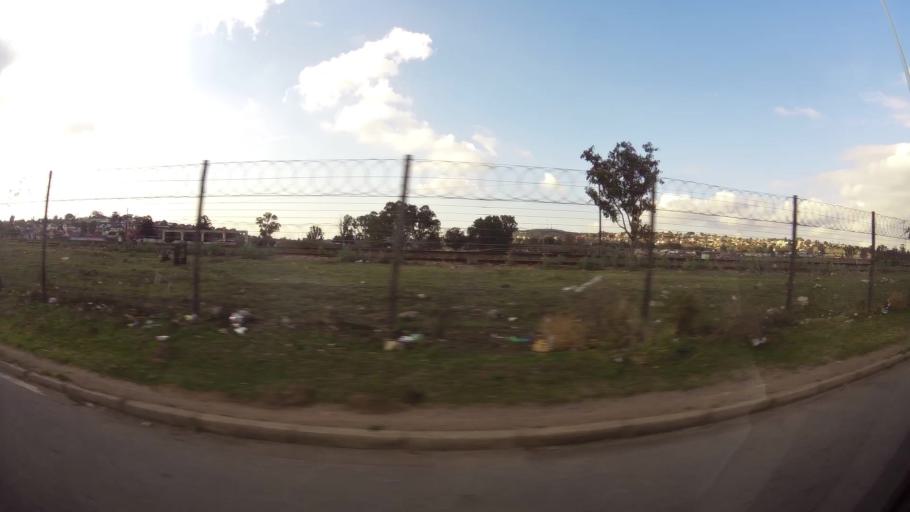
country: ZA
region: Eastern Cape
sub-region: Nelson Mandela Bay Metropolitan Municipality
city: Uitenhage
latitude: -33.7763
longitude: 25.4063
